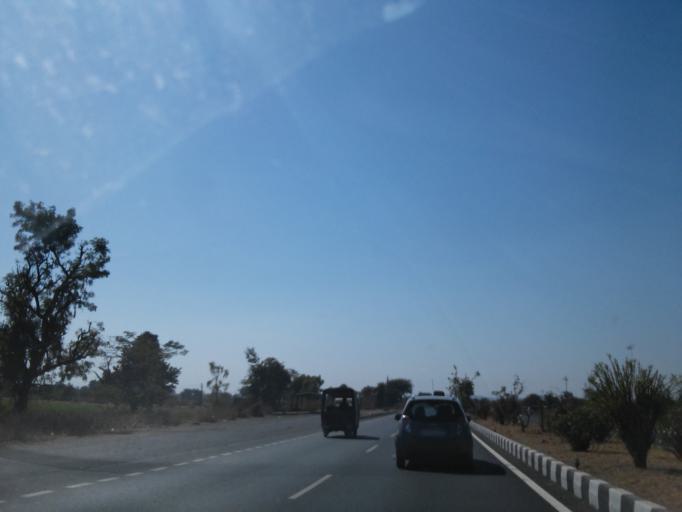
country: IN
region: Gujarat
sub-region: Sabar Kantha
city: Modasa
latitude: 23.6404
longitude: 73.3069
